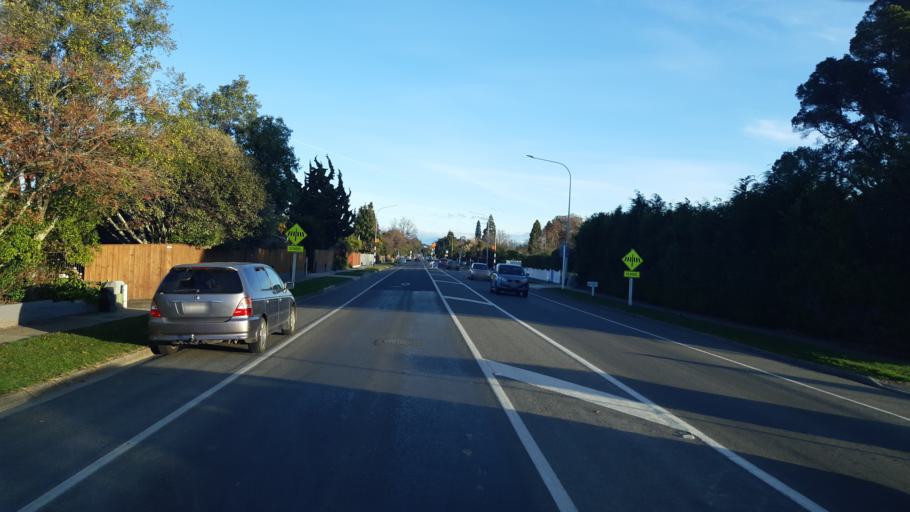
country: NZ
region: Tasman
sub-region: Tasman District
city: Motueka
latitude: -41.1263
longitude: 173.0103
